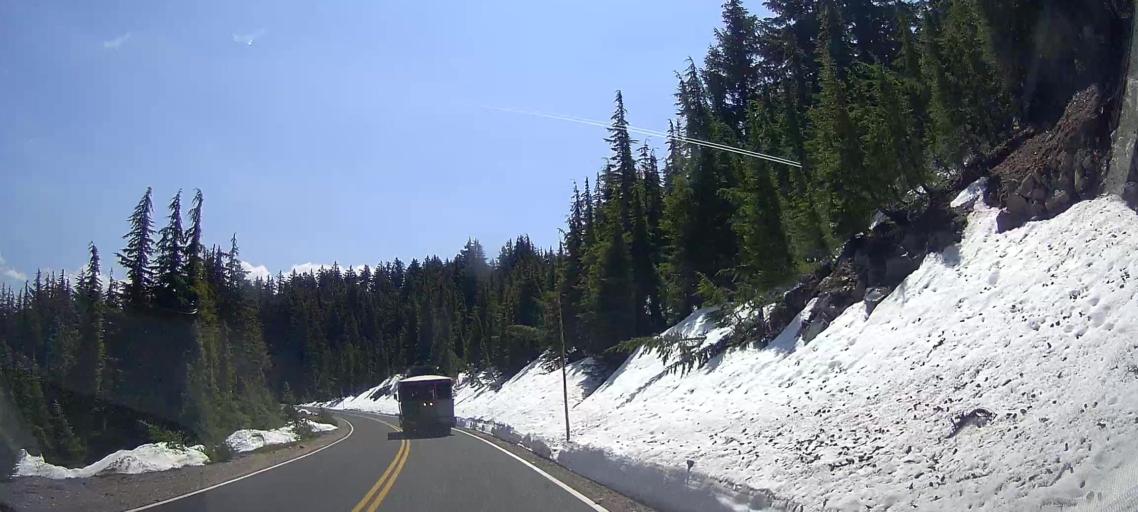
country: US
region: Oregon
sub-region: Jackson County
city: Shady Cove
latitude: 42.9806
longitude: -122.1283
